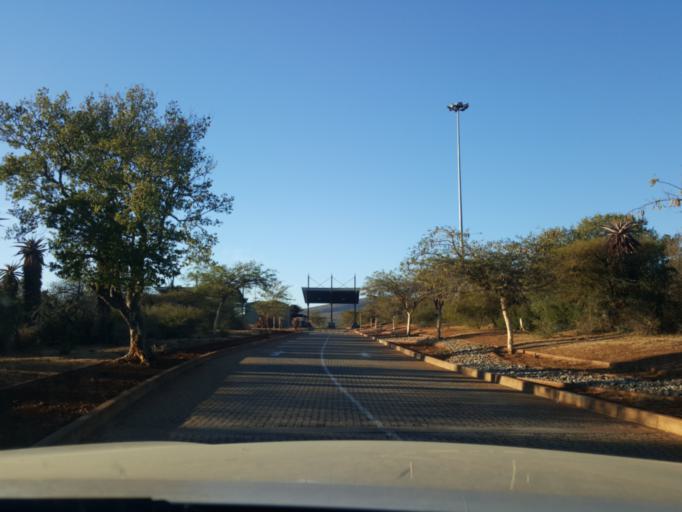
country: BW
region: South East
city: Lobatse
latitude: -25.2792
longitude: 25.7164
